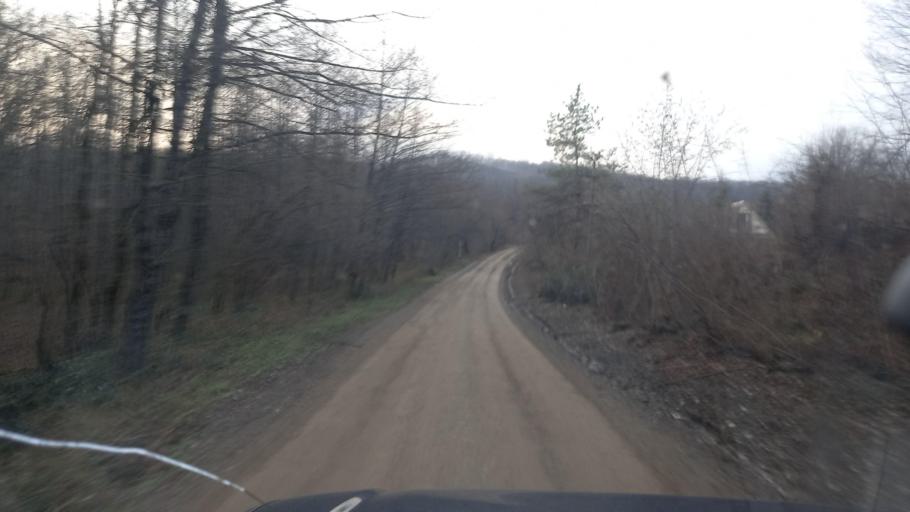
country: RU
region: Krasnodarskiy
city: Goryachiy Klyuch
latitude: 44.3785
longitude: 39.1955
